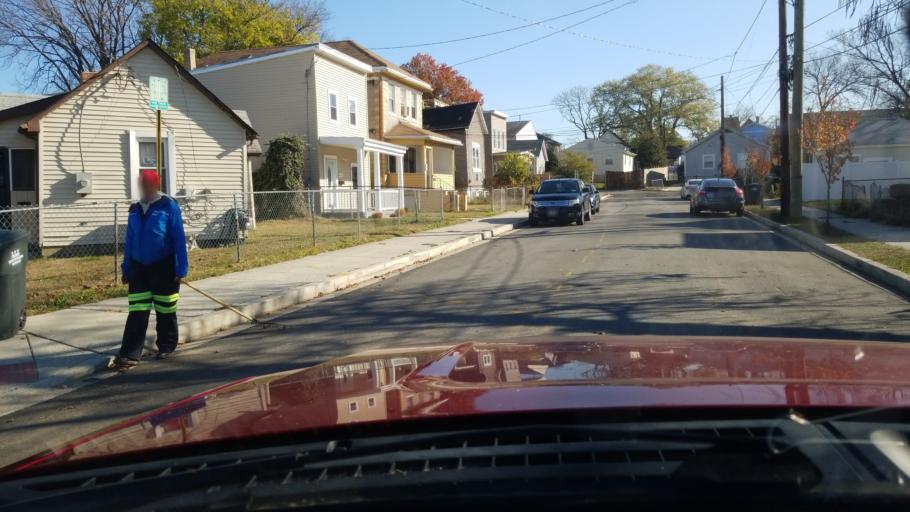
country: US
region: Maryland
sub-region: Prince George's County
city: Fairmount Heights
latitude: 38.9036
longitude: -76.9403
